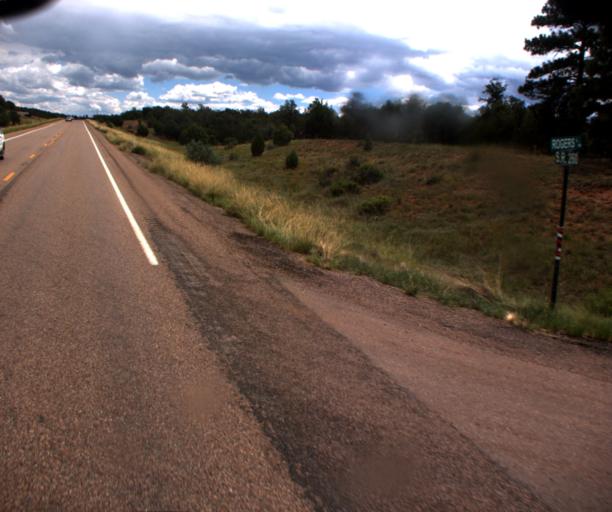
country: US
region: Arizona
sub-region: Navajo County
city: Linden
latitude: 34.3463
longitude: -110.2983
